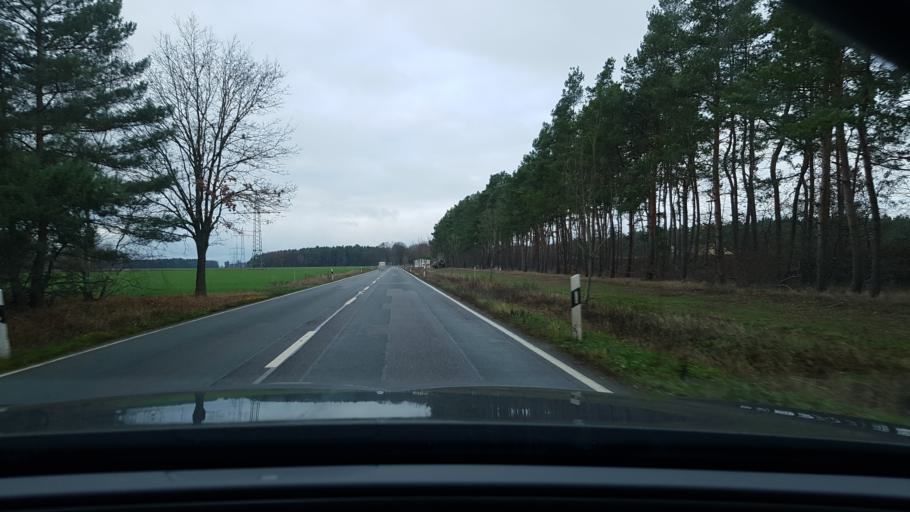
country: DE
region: Lower Saxony
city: Bahrdorf
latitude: 52.4164
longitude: 11.0574
